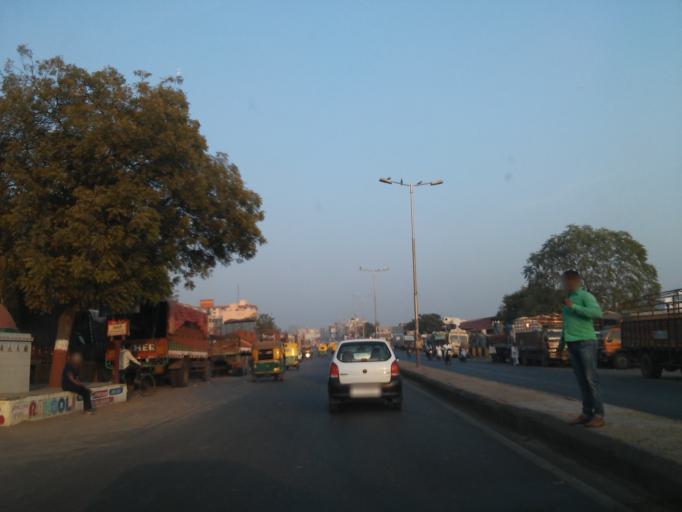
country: IN
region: Gujarat
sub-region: Ahmadabad
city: Sarkhej
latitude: 22.9883
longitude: 72.5078
